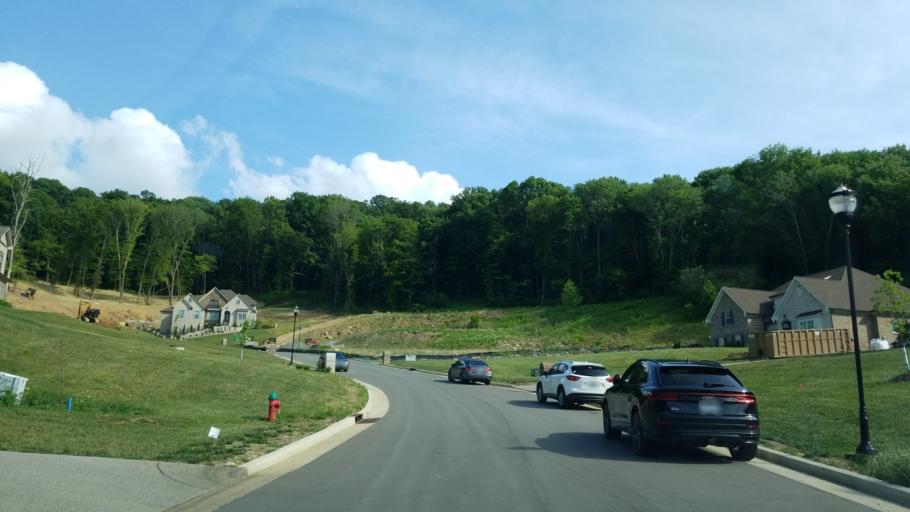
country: US
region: Tennessee
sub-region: Davidson County
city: Forest Hills
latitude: 36.0368
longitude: -86.8548
